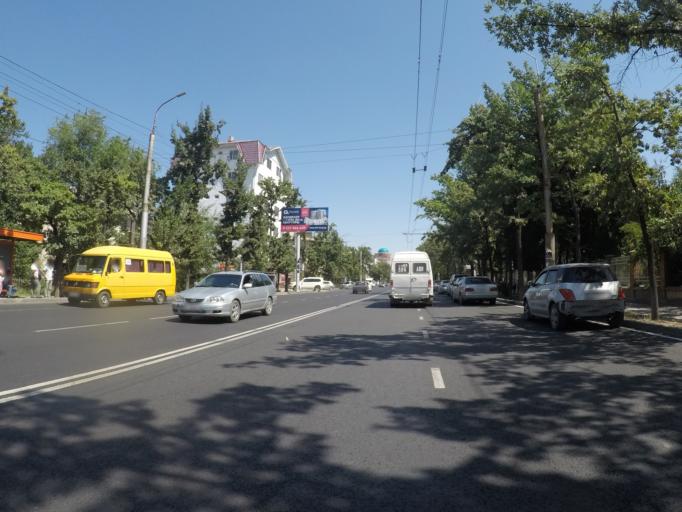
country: KG
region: Chuy
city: Bishkek
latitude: 42.8436
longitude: 74.5841
